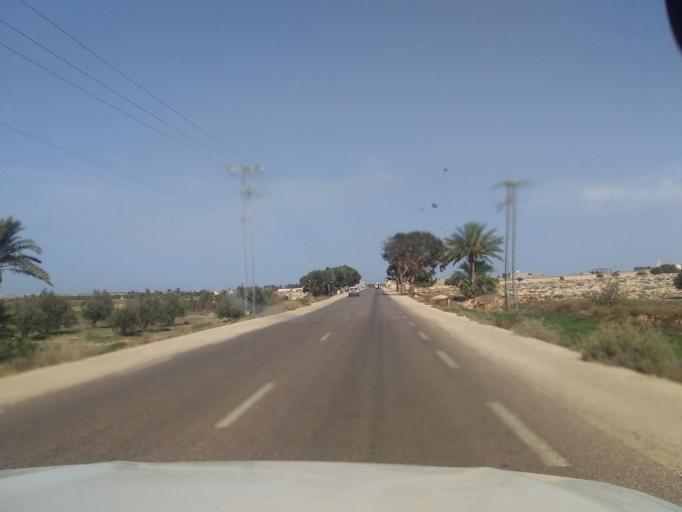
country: TN
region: Qabis
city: Gabes
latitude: 33.6404
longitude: 10.2901
